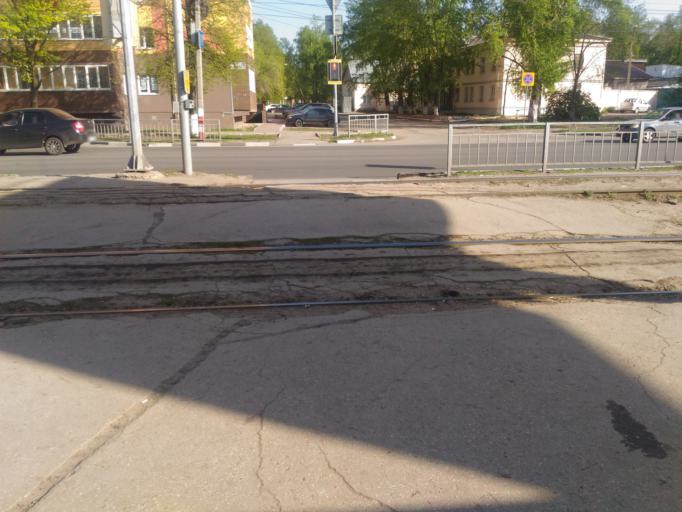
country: RU
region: Ulyanovsk
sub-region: Ulyanovskiy Rayon
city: Ulyanovsk
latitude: 54.2772
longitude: 48.3391
